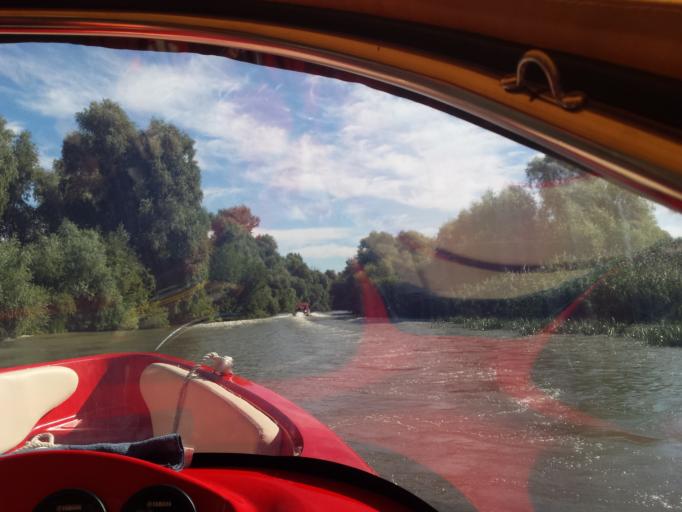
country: RO
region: Tulcea
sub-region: Comuna Pardina
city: Pardina
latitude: 45.2464
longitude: 29.0145
